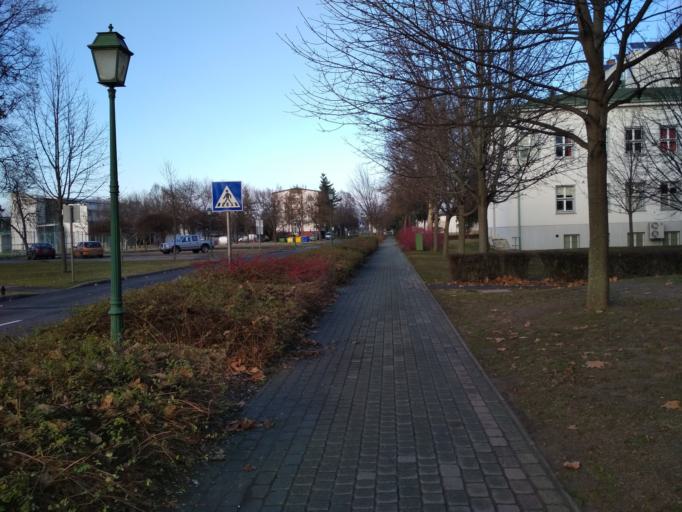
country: HU
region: Hajdu-Bihar
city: Debrecen
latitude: 47.5492
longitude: 21.6082
